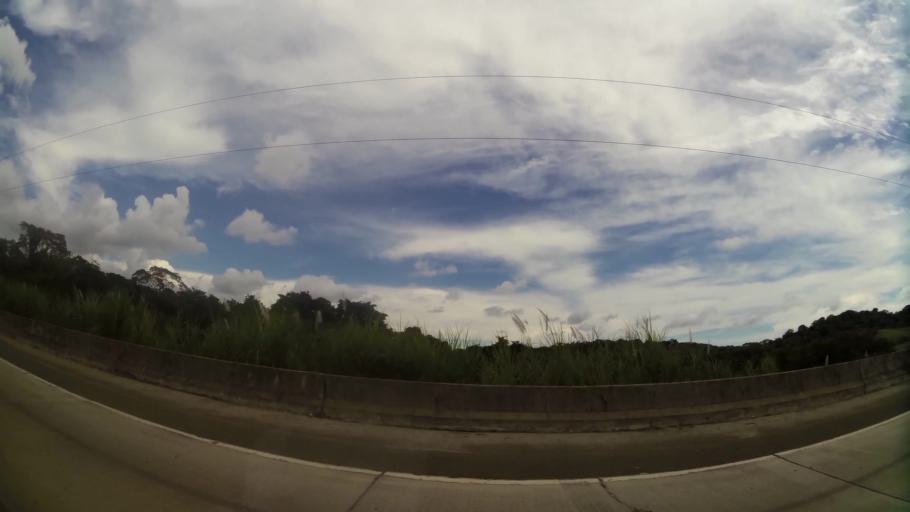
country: PA
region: Panama
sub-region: Distrito Arraijan
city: Arraijan
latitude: 8.9719
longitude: -79.6434
